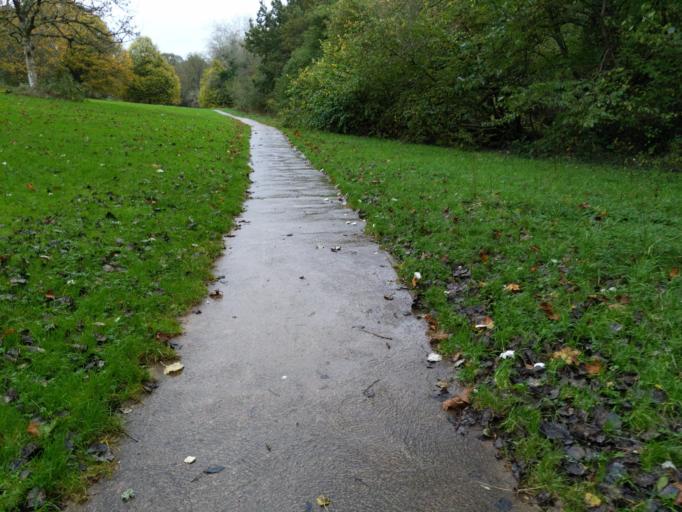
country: GB
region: England
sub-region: Plymouth
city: Plymouth
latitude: 50.4147
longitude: -4.1502
